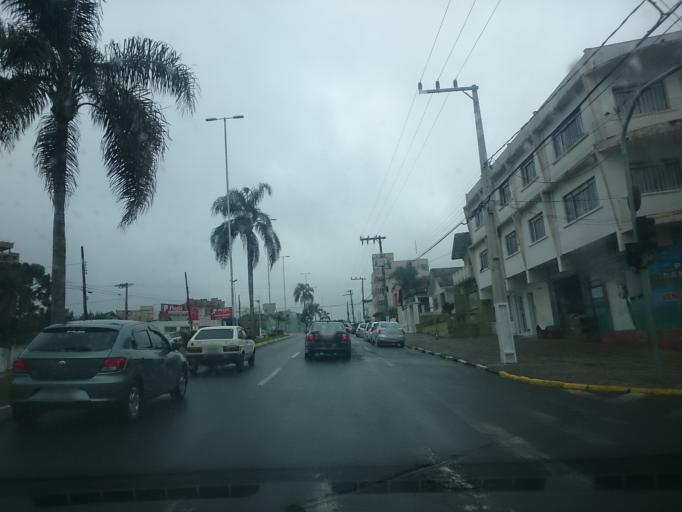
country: BR
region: Santa Catarina
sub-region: Lages
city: Lages
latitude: -27.8190
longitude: -50.3323
